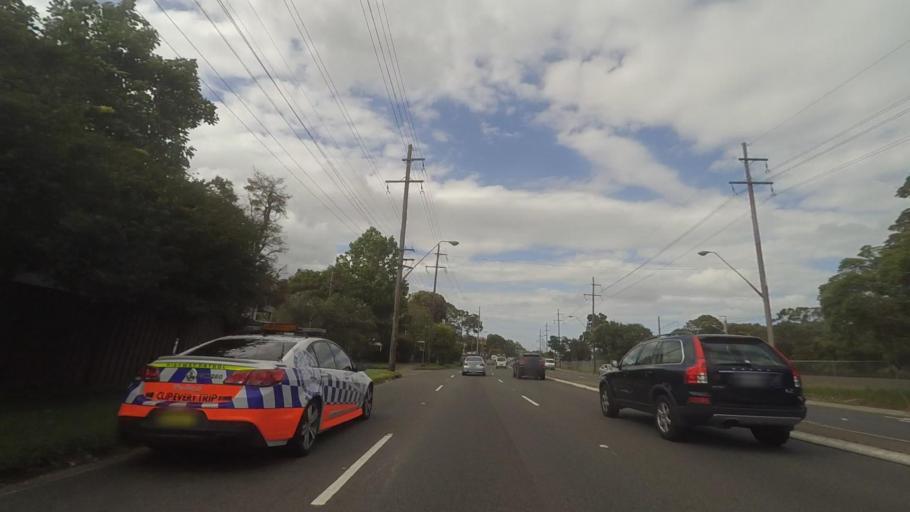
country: AU
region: New South Wales
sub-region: Sutherland Shire
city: Engadine
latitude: -34.0709
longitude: 151.0124
